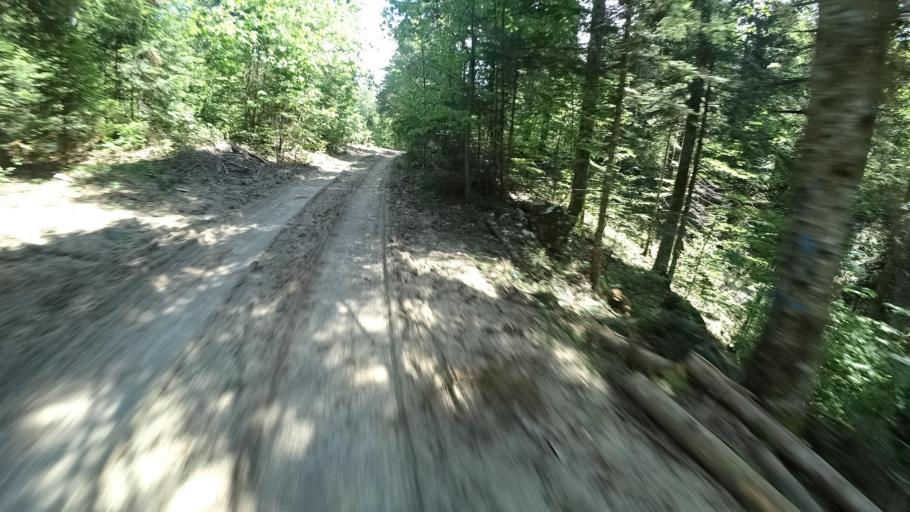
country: BA
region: Federation of Bosnia and Herzegovina
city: Stijena
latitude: 44.8142
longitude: 16.0219
